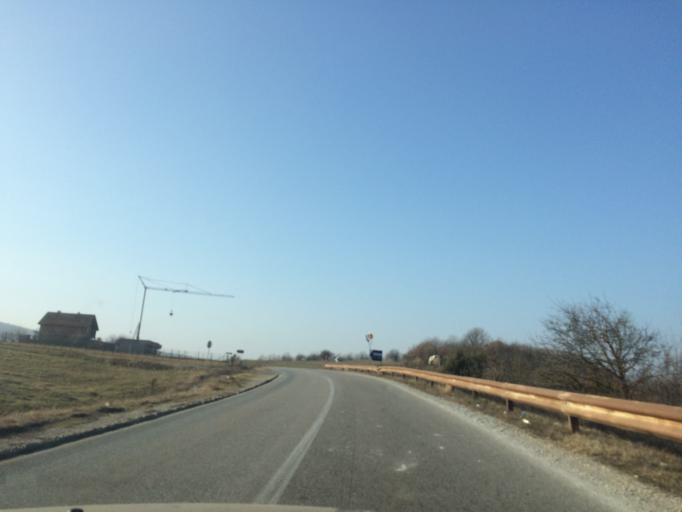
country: XK
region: Pec
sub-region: Komuna e Pejes
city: Kosuriq
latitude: 42.5143
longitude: 20.5505
